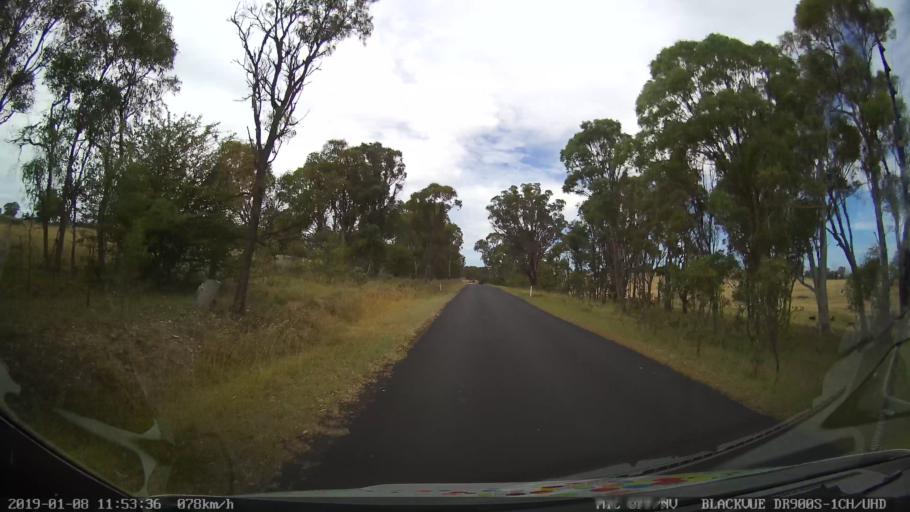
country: AU
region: New South Wales
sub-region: Armidale Dumaresq
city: Armidale
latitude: -30.4164
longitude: 151.5616
